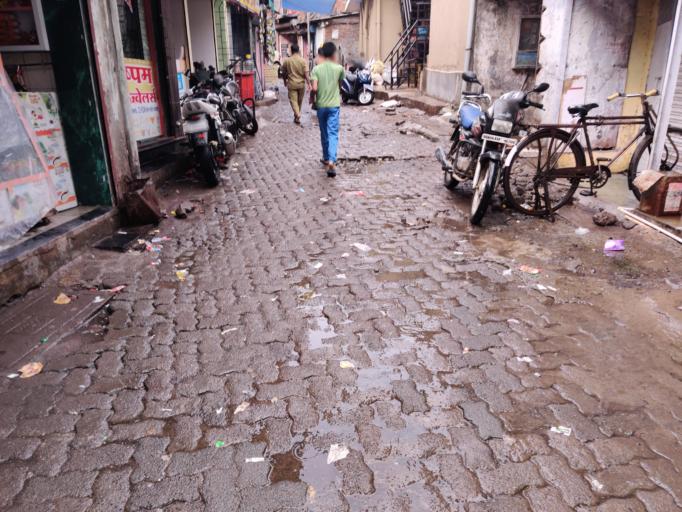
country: IN
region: Maharashtra
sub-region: Mumbai Suburban
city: Borivli
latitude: 19.2447
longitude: 72.8546
